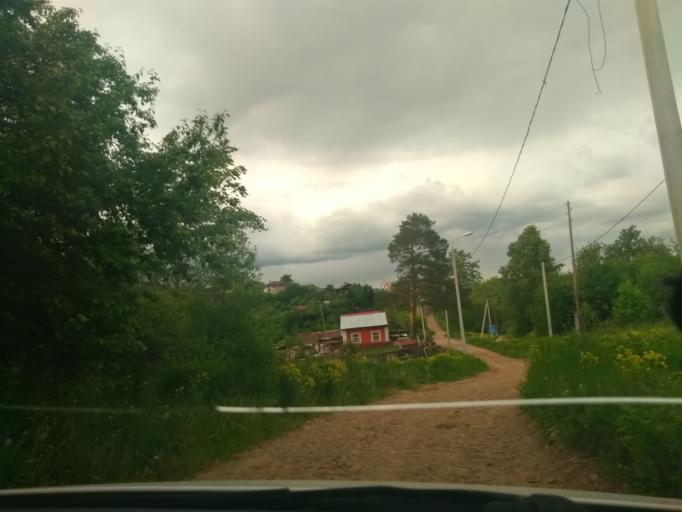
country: RU
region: Perm
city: Perm
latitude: 57.9889
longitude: 56.3367
